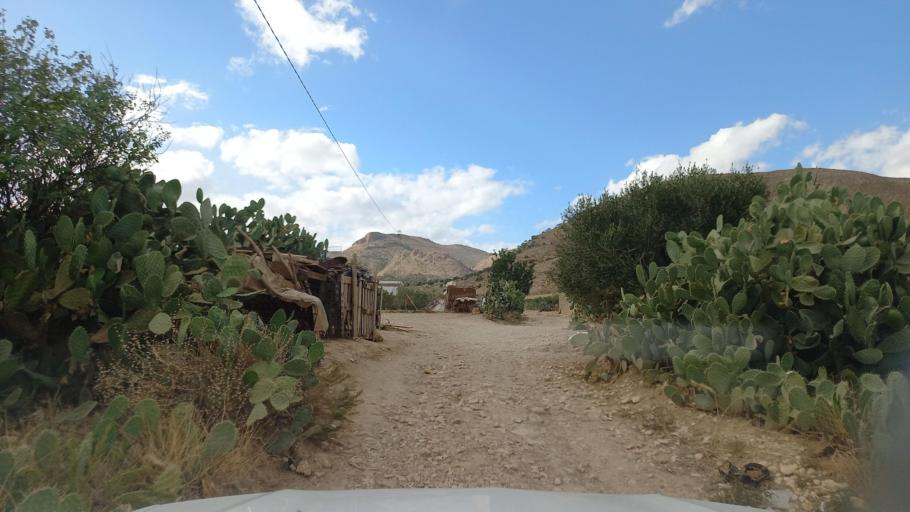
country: TN
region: Al Qasrayn
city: Sbiba
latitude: 35.4515
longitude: 9.0644
